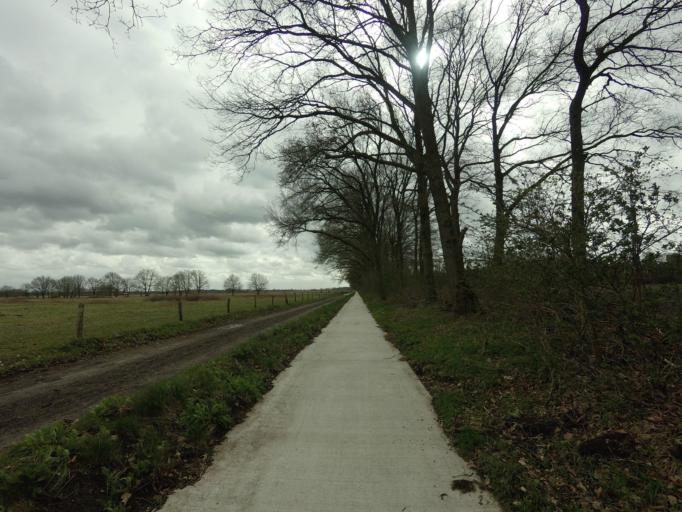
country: NL
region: Gelderland
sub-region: Gemeente Renkum
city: Heelsum
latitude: 52.0055
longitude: 5.7485
